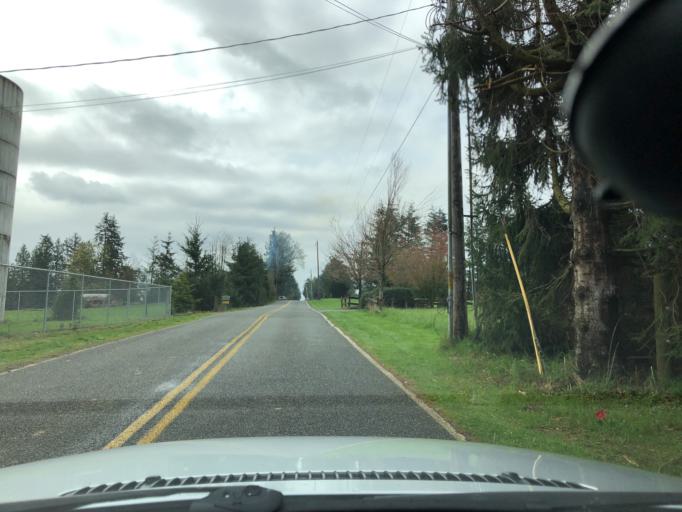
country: US
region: Washington
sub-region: Whatcom County
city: Lynden
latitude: 48.9922
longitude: -122.5183
